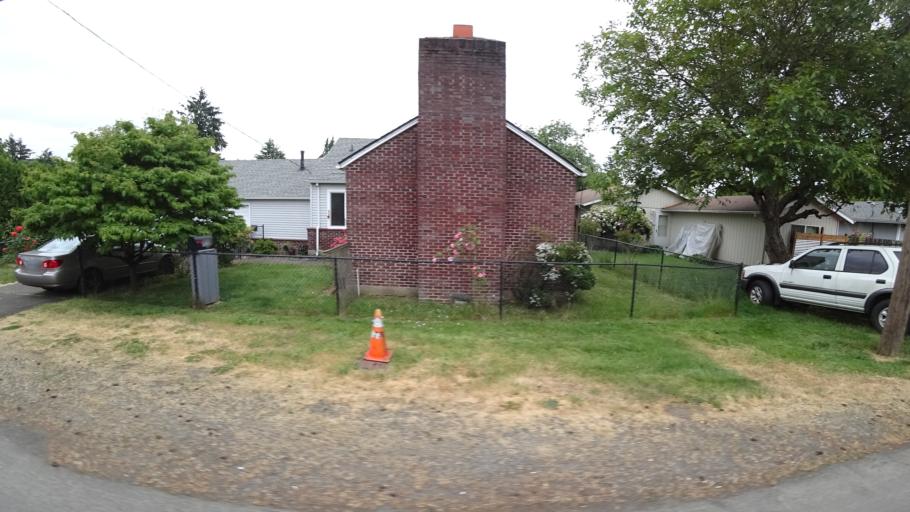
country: US
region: Oregon
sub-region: Multnomah County
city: Lents
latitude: 45.4710
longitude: -122.5843
